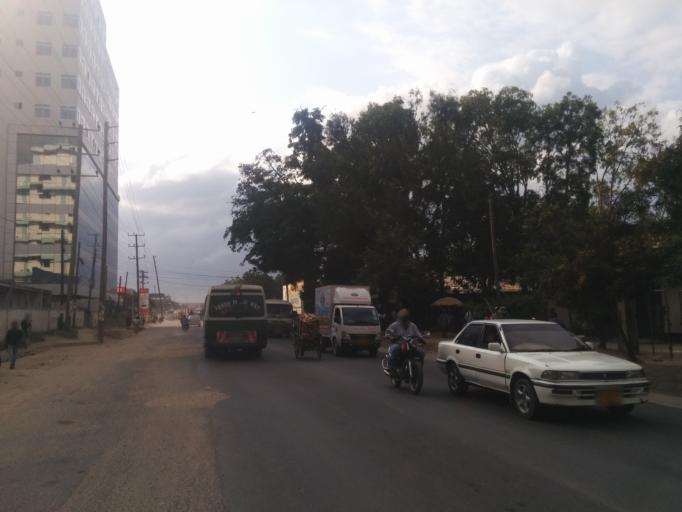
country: TZ
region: Dar es Salaam
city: Dar es Salaam
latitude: -6.8340
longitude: 39.2696
